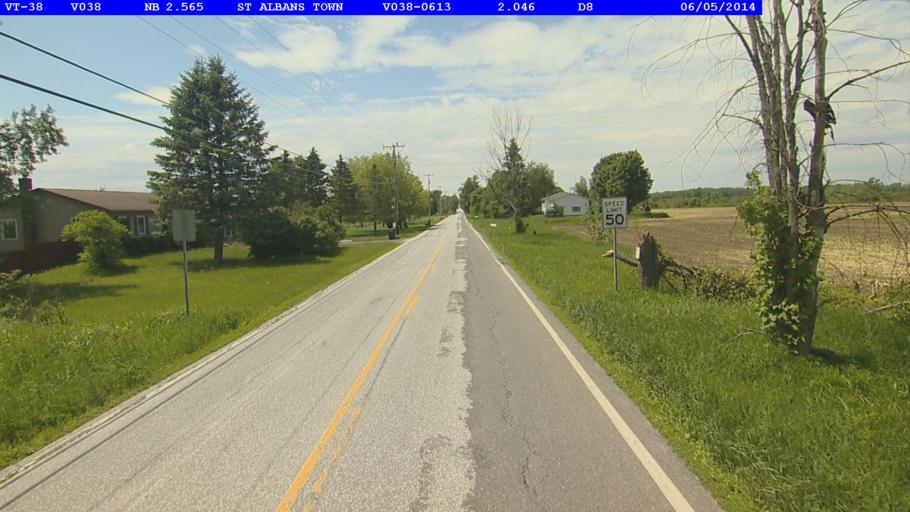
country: US
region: Vermont
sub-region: Franklin County
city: Saint Albans
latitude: 44.8471
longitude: -73.1138
